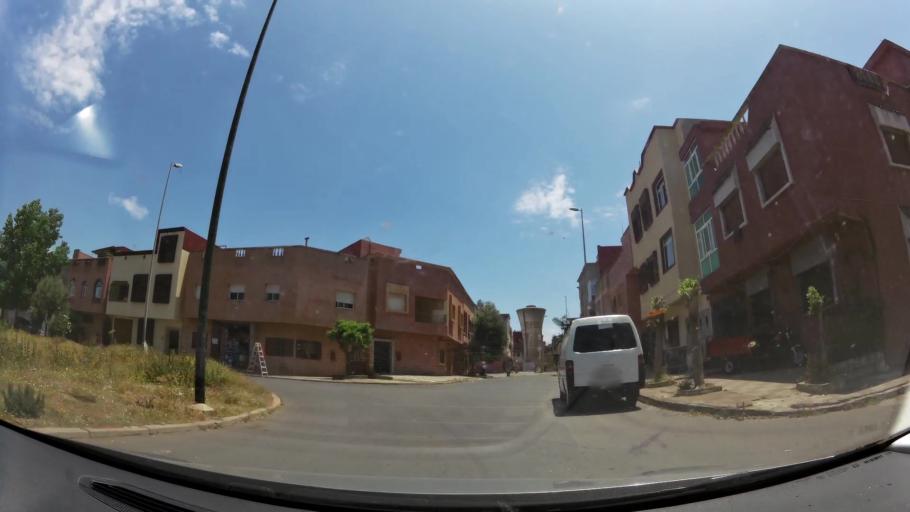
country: MA
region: Gharb-Chrarda-Beni Hssen
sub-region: Kenitra Province
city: Kenitra
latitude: 34.2679
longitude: -6.6218
